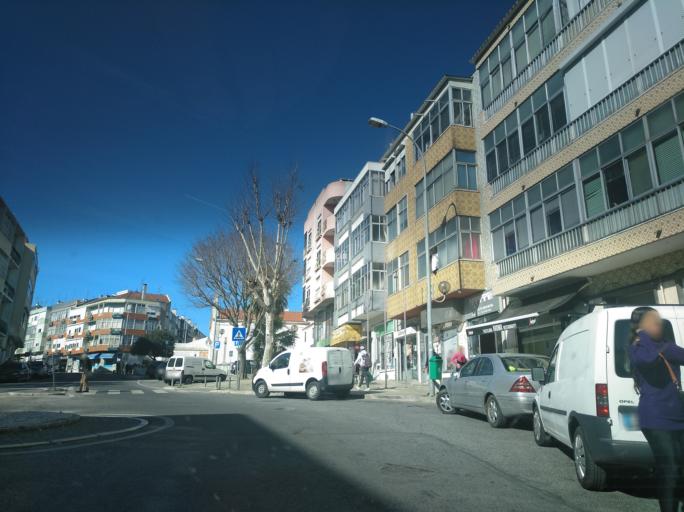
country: PT
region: Lisbon
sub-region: Amadora
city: Amadora
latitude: 38.7588
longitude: -9.2264
